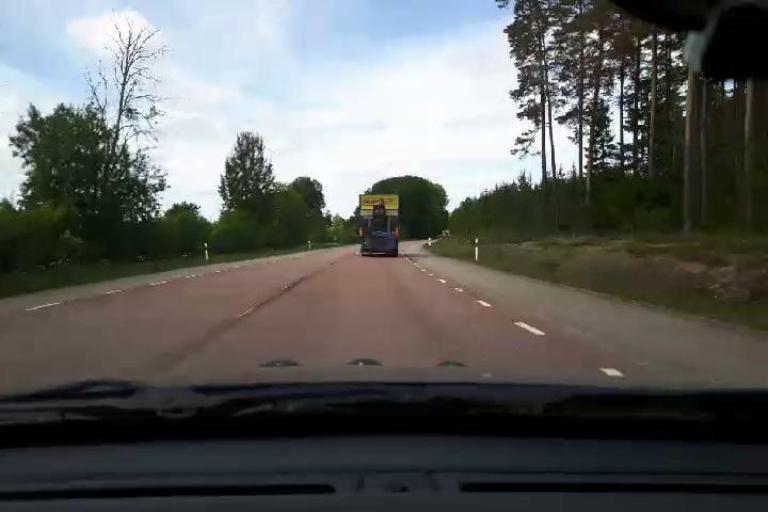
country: SE
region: Uppsala
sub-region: Osthammars Kommun
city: Bjorklinge
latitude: 60.1489
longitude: 17.4950
